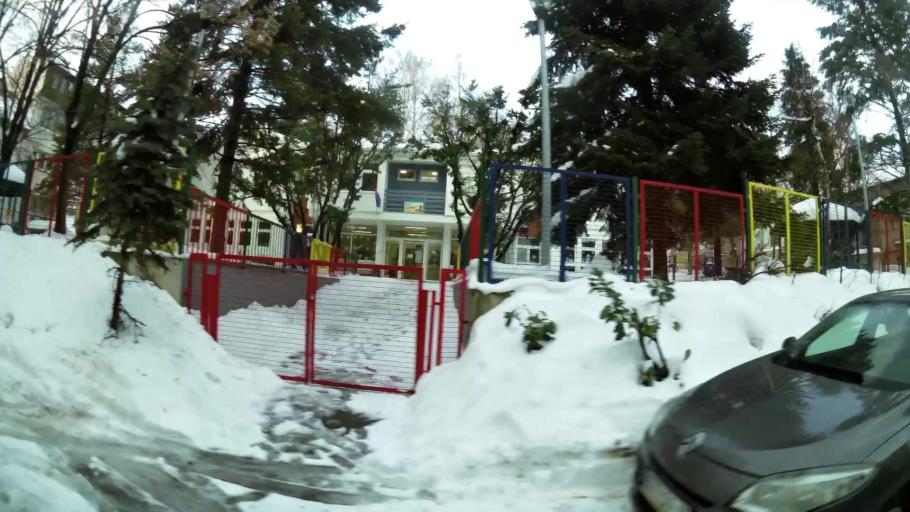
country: RS
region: Central Serbia
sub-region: Belgrade
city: Palilula
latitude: 44.7922
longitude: 20.5122
